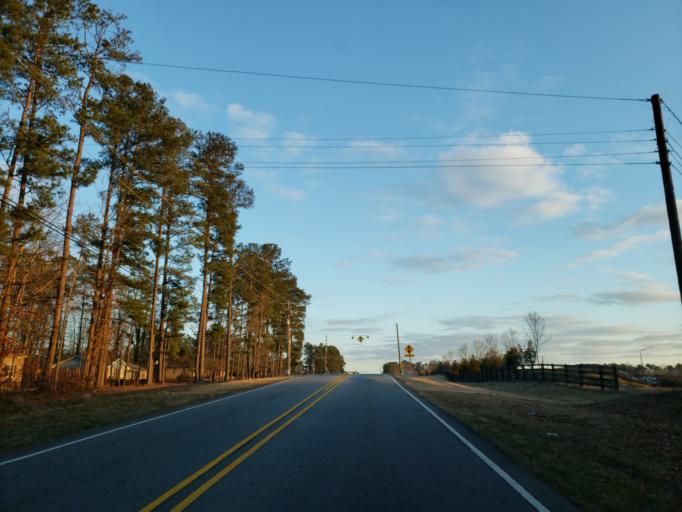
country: US
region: Georgia
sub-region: Cobb County
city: Acworth
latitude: 33.9772
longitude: -84.7152
